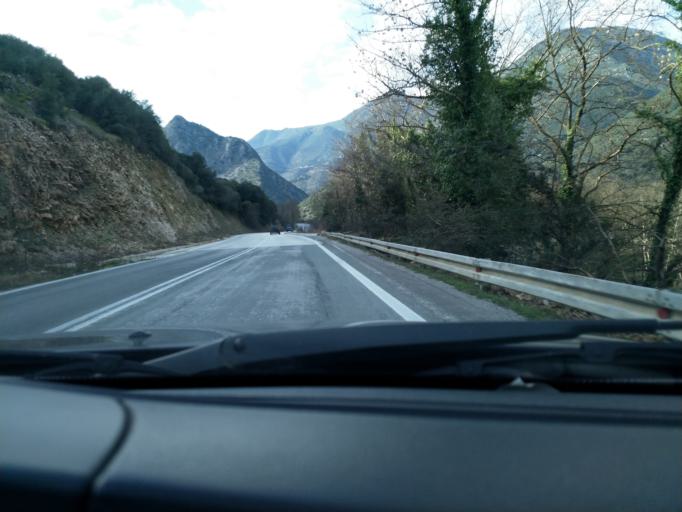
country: GR
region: Epirus
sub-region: Nomos Prevezis
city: Pappadates
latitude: 39.4104
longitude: 20.8413
